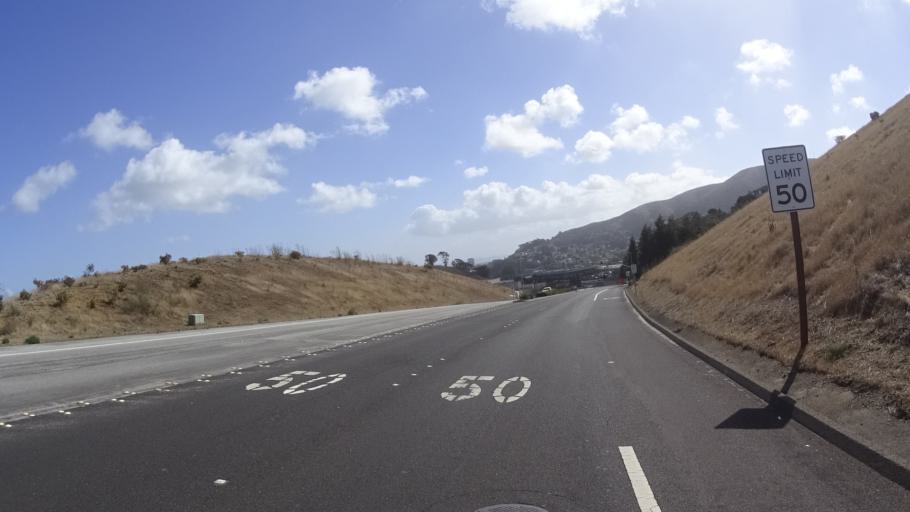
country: US
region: California
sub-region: San Mateo County
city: Brisbane
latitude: 37.6966
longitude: -122.4091
